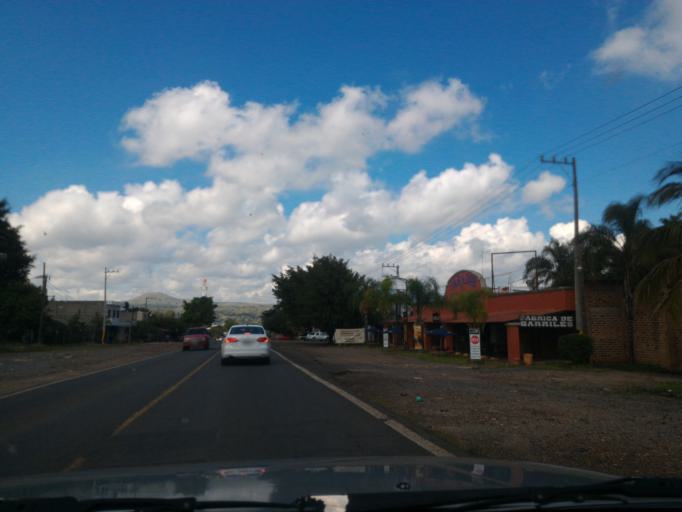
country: MX
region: Jalisco
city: Tequila
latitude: 20.8778
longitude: -103.8176
